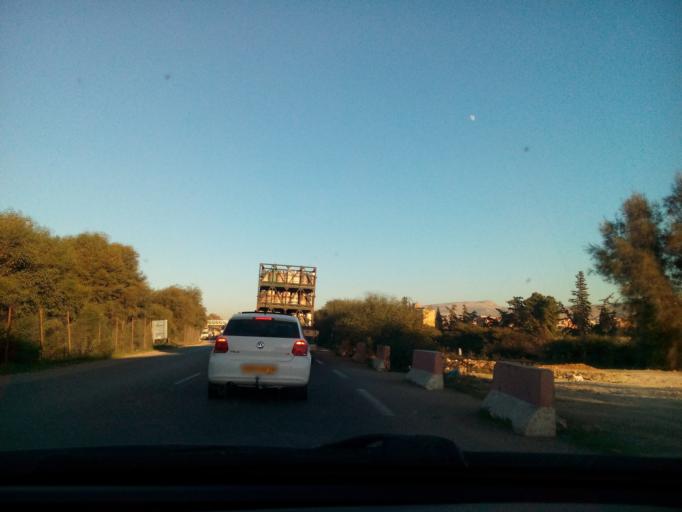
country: DZ
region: Relizane
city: Oued Rhiou
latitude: 35.9679
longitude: 0.9069
